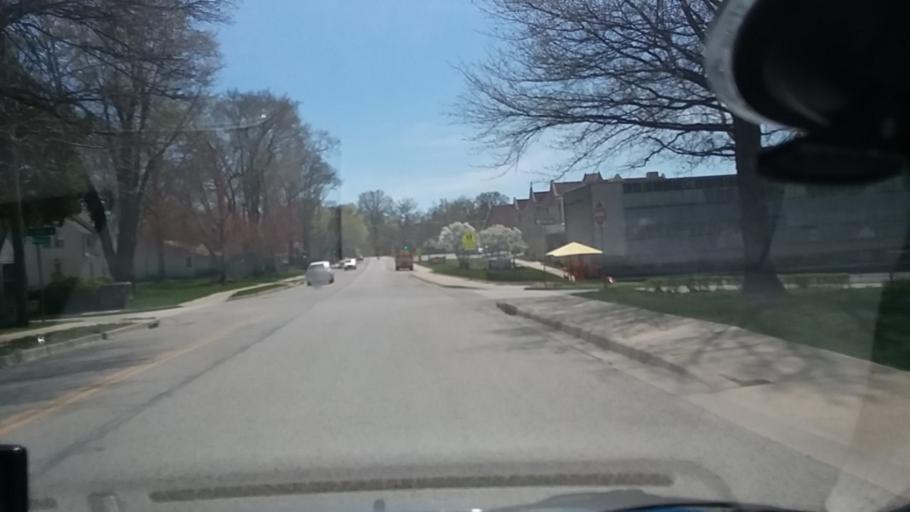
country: US
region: Kansas
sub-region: Johnson County
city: Westwood
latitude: 39.0359
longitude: -94.6212
